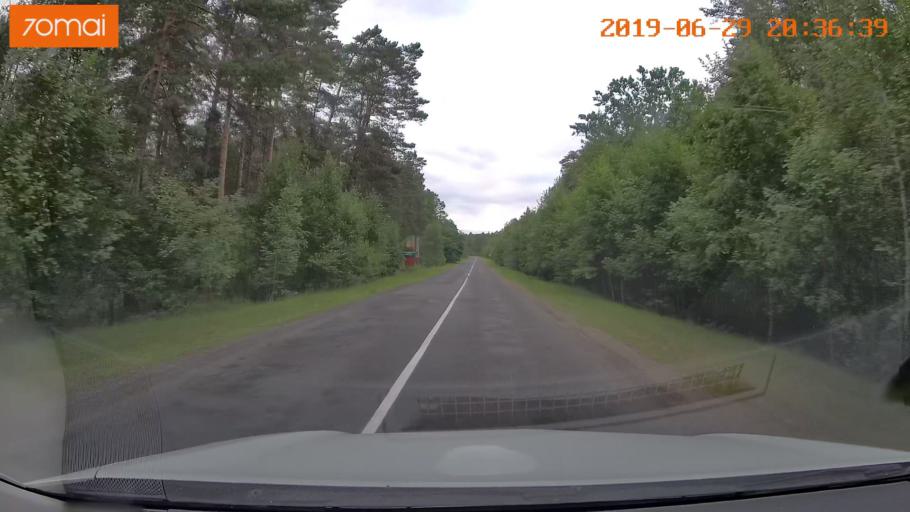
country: BY
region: Brest
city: Hantsavichy
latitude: 52.5286
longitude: 26.3601
